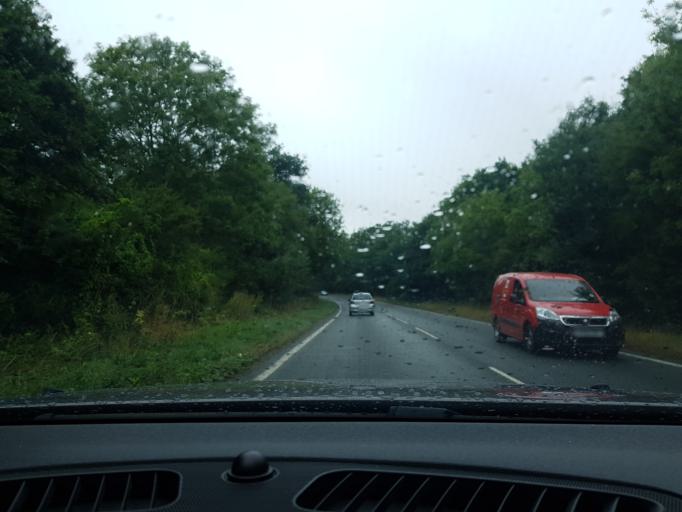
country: GB
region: England
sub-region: Hampshire
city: Odiham
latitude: 51.2511
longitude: -0.9000
